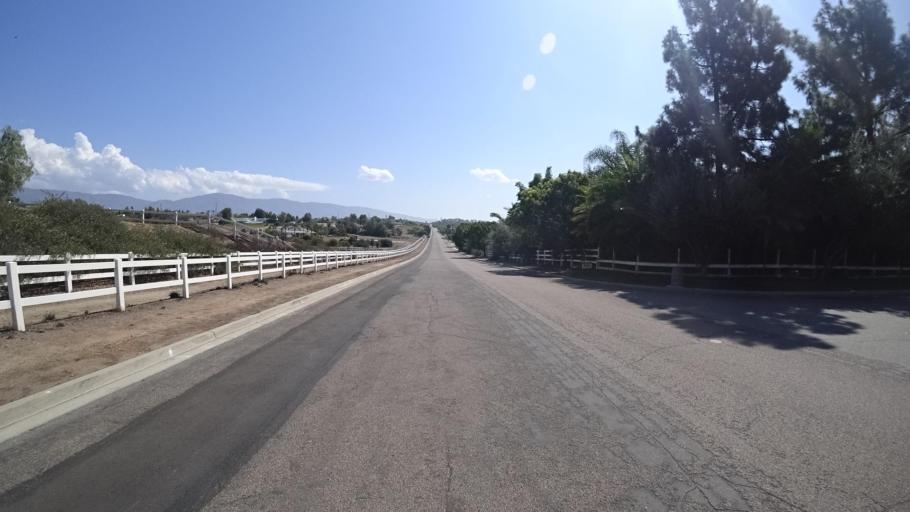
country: US
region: California
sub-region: San Diego County
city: Valley Center
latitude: 33.2820
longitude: -117.0193
